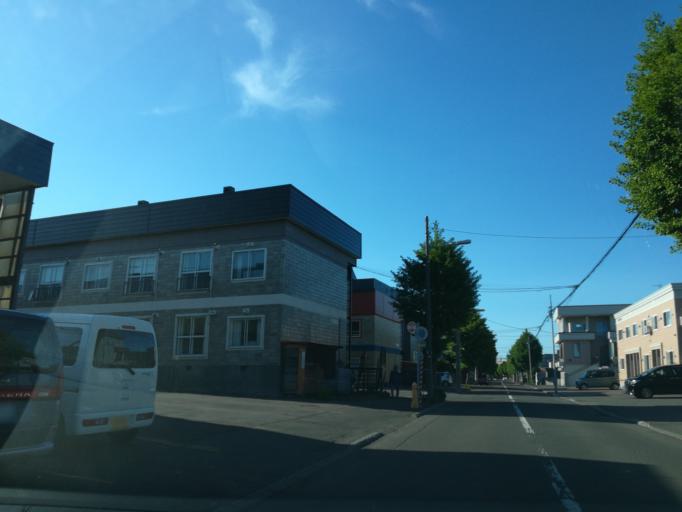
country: JP
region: Hokkaido
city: Sapporo
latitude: 43.0200
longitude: 141.4328
